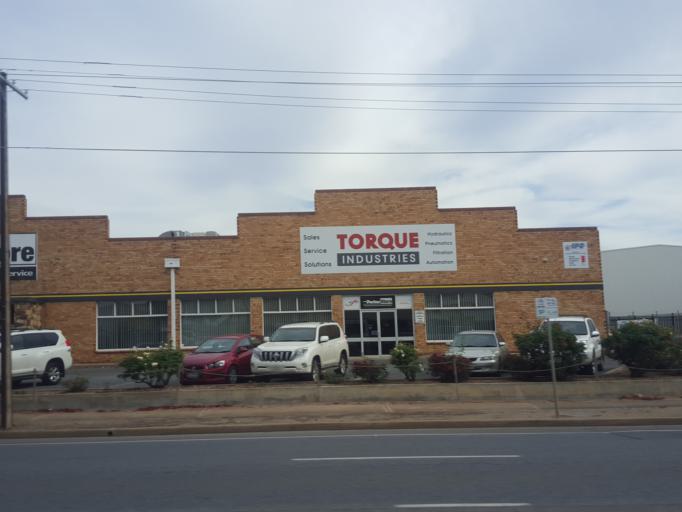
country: AU
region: South Australia
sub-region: Port Adelaide Enfield
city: Alberton
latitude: -34.8509
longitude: 138.5400
